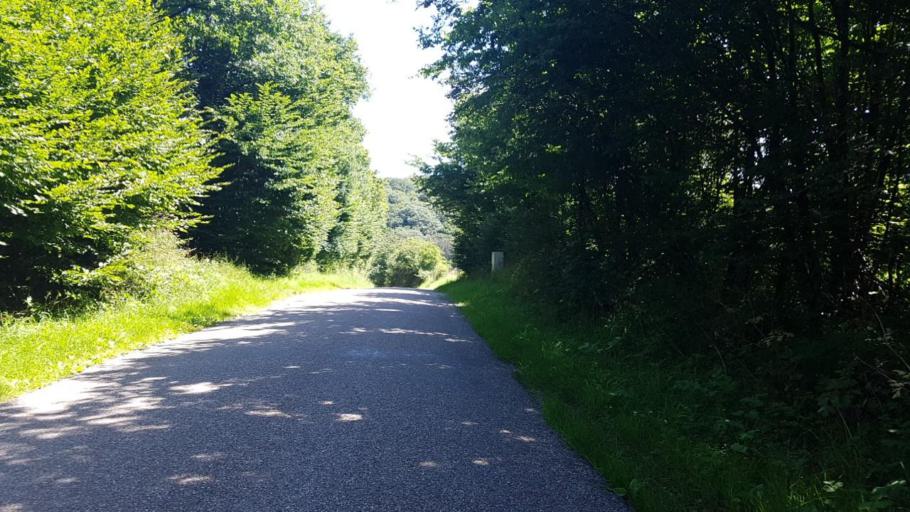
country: BE
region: Wallonia
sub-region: Province du Hainaut
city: Froidchapelle
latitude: 50.1298
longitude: 4.2536
